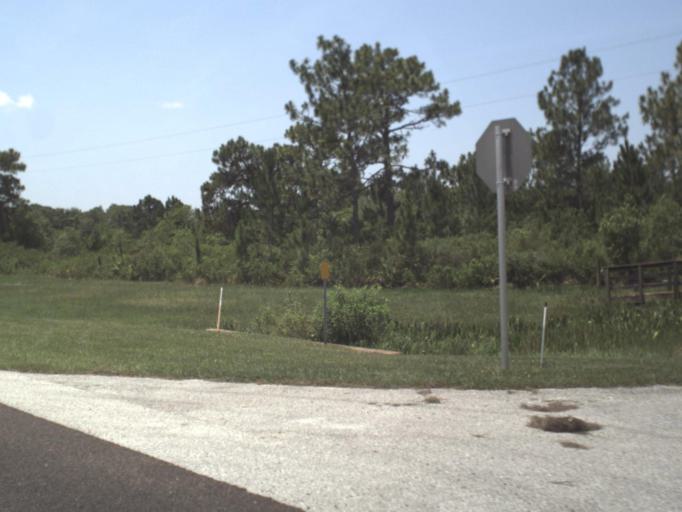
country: US
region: Florida
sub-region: Citrus County
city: Sugarmill Woods
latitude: 28.7053
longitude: -82.5527
